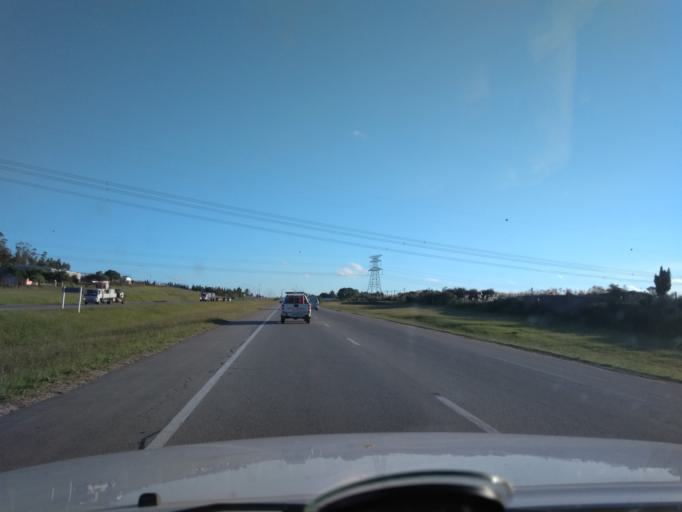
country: UY
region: Canelones
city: La Paz
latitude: -34.7607
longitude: -56.2621
